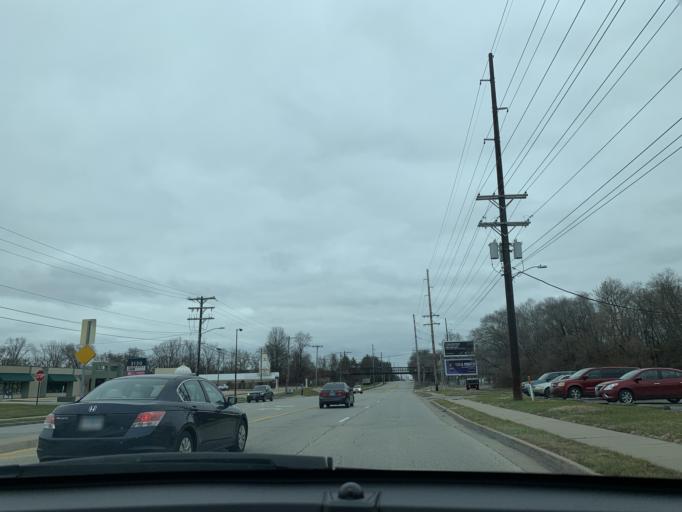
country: US
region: Illinois
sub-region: Sangamon County
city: Jerome
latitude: 39.7630
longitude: -89.6869
